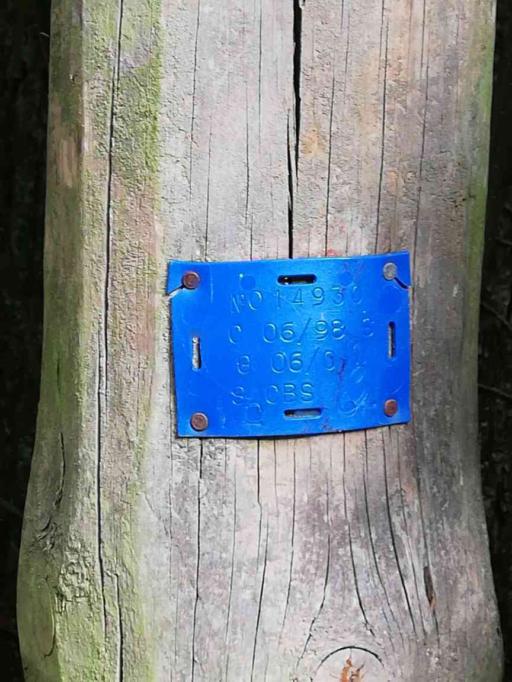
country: FR
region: Pays de la Loire
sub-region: Departement de la Vendee
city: Le Champ-Saint-Pere
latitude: 46.4996
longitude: -1.3458
